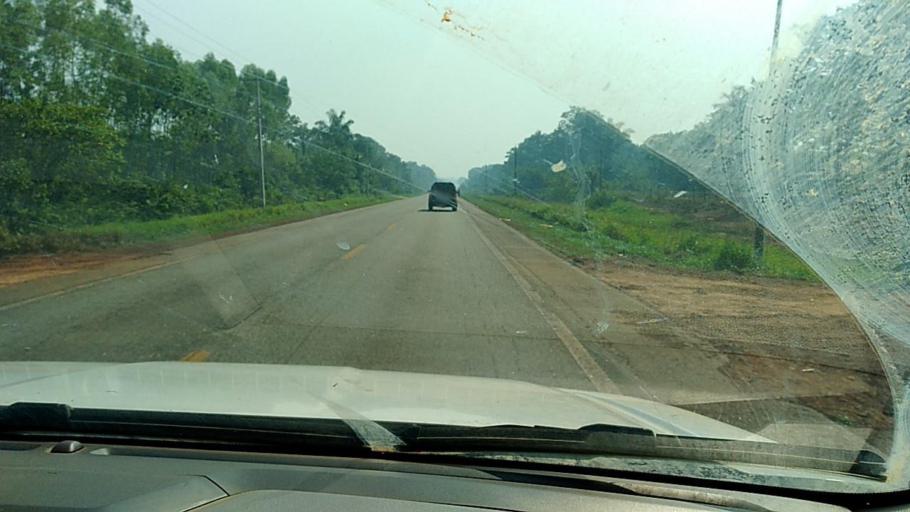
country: BR
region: Amazonas
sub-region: Humaita
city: Humaita
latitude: -7.8202
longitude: -63.1949
